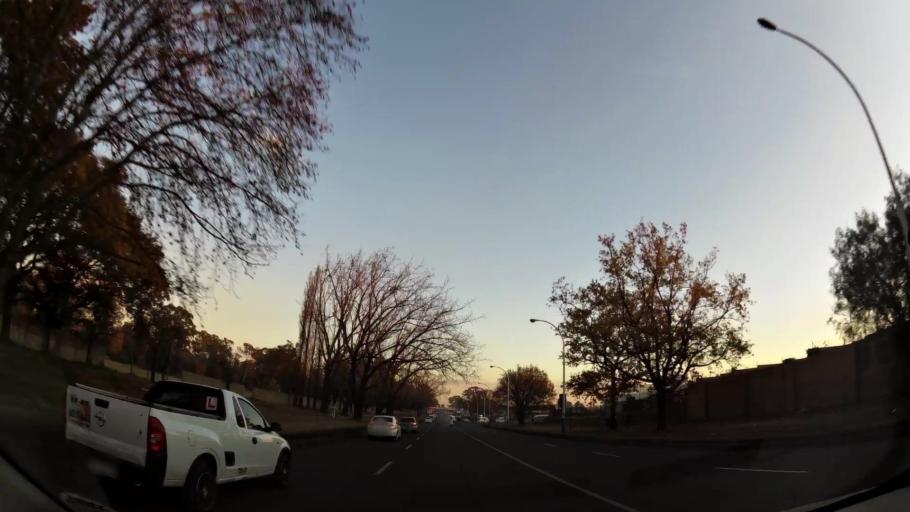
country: ZA
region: Mpumalanga
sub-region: Nkangala District Municipality
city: Witbank
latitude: -25.8803
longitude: 29.2089
